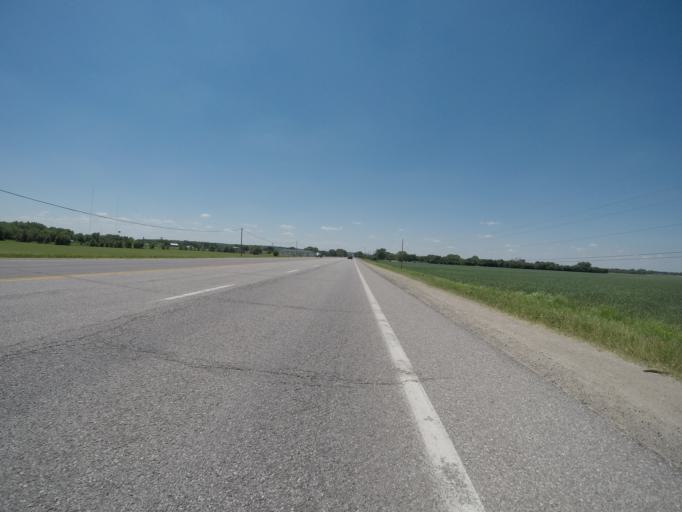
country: US
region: Kansas
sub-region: Geary County
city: Grandview Plaza
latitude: 39.0283
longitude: -96.8072
